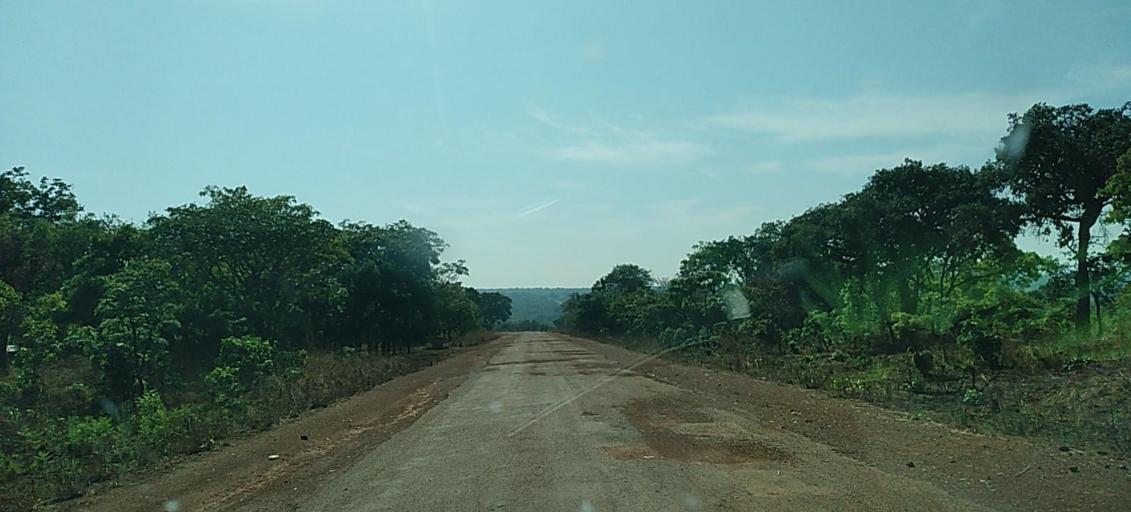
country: ZM
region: North-Western
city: Mwinilunga
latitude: -11.8233
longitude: 25.1162
